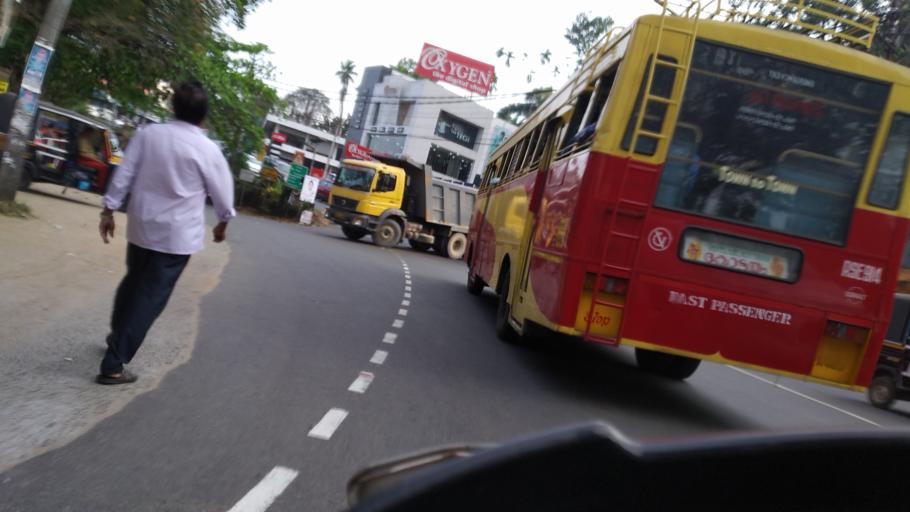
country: IN
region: Kerala
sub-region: Kottayam
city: Erattupetta
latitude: 9.5550
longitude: 76.7900
